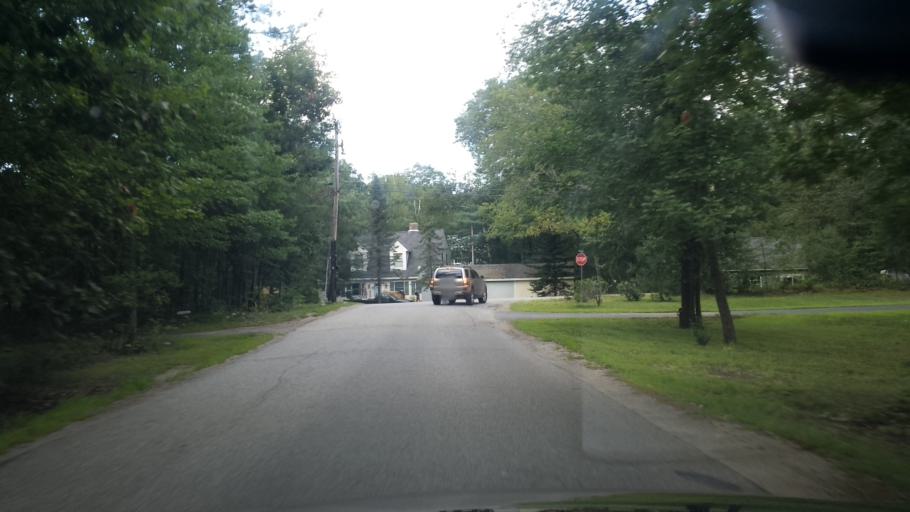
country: US
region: Maine
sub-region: York County
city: Dayton
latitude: 43.5008
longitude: -70.6366
